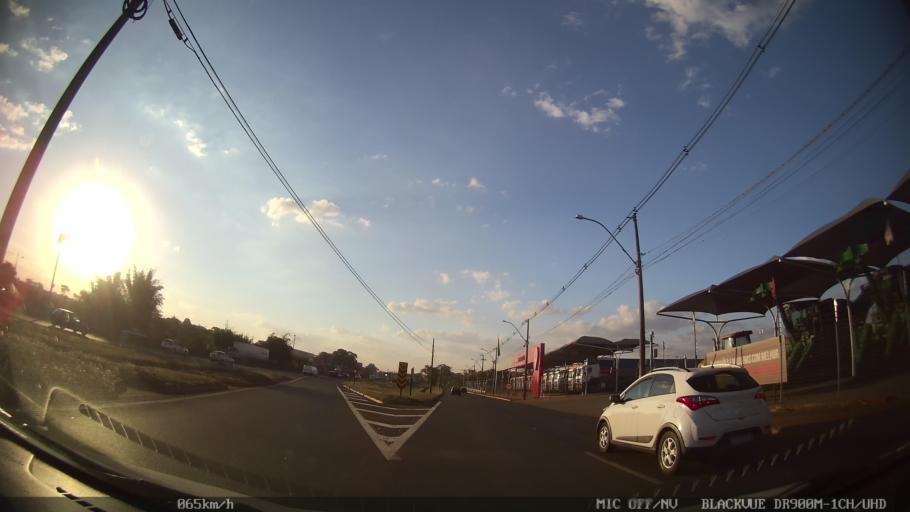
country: BR
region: Sao Paulo
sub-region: Ribeirao Preto
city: Ribeirao Preto
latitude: -21.1585
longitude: -47.7560
